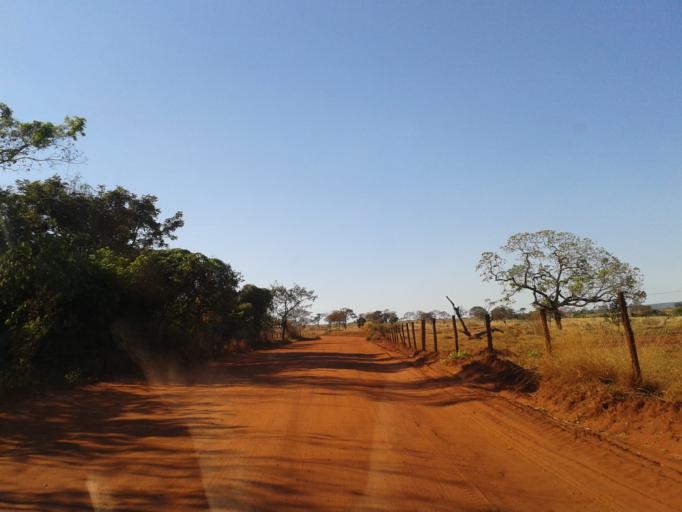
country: BR
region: Minas Gerais
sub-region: Ituiutaba
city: Ituiutaba
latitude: -18.9894
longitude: -49.3866
